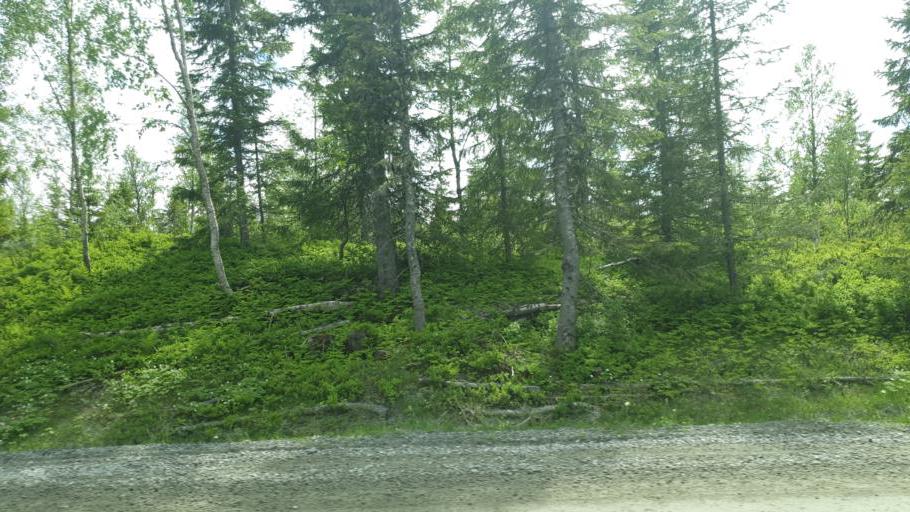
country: NO
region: Nord-Trondelag
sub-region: Leksvik
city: Leksvik
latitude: 63.6912
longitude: 10.4626
